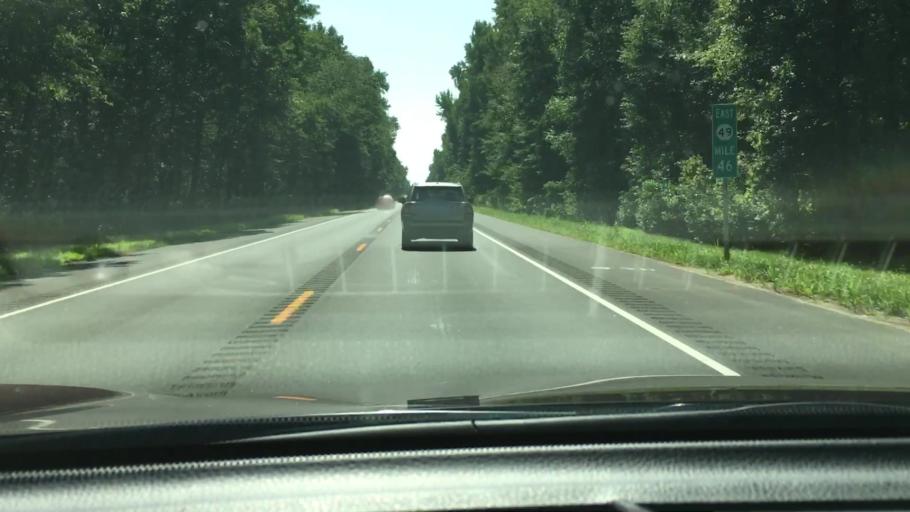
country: US
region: New Jersey
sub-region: Cape May County
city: Woodbine
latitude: 39.3335
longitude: -74.8806
